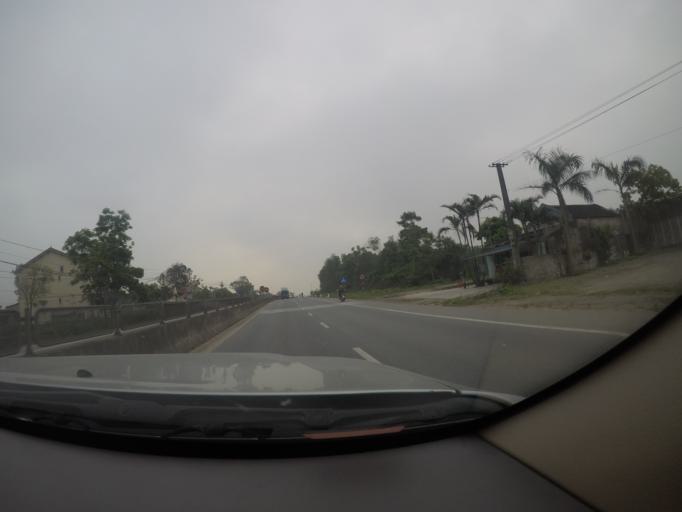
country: VN
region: Ha Tinh
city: Cam Xuyen
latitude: 18.2029
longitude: 106.1528
